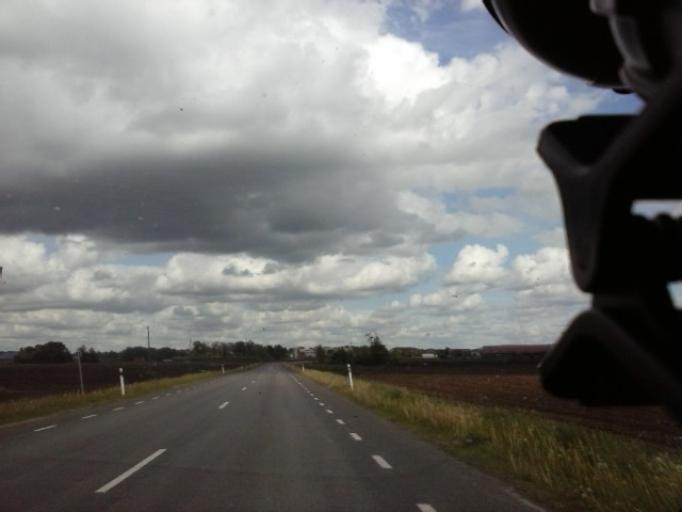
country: EE
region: Jogevamaa
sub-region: Poltsamaa linn
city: Poltsamaa
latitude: 58.6396
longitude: 25.8689
